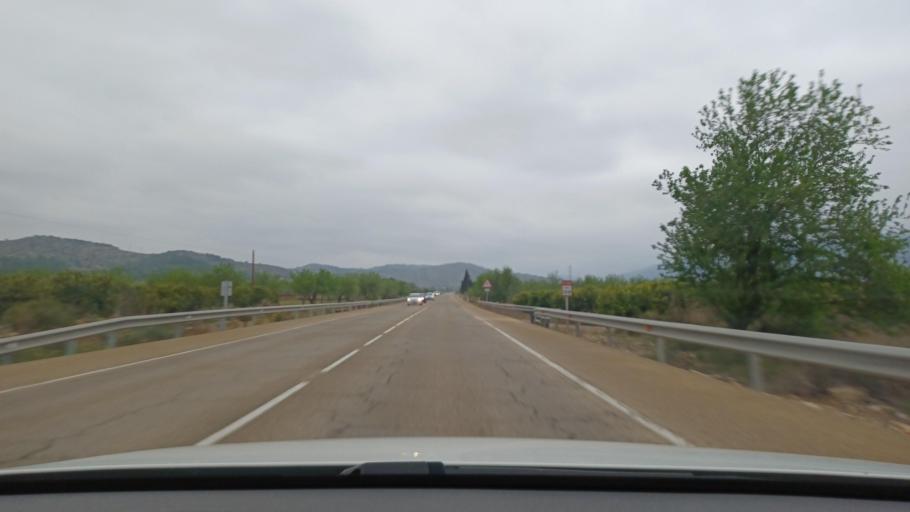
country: ES
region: Valencia
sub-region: Provincia de Castello
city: Torreblanca
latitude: 40.2491
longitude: 0.2336
